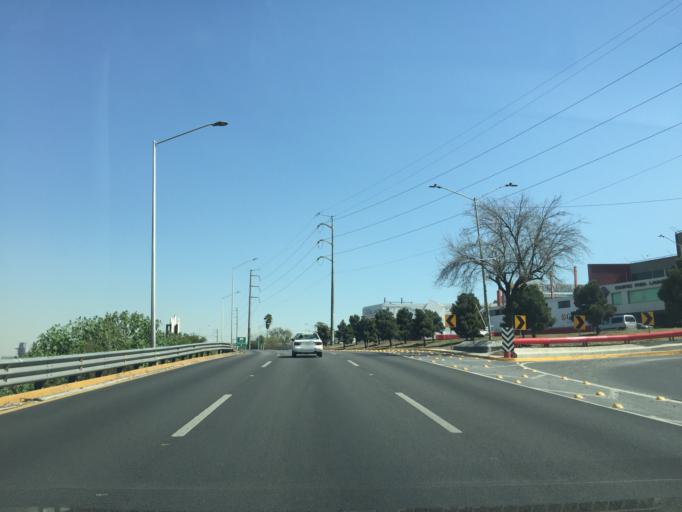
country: MX
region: Nuevo Leon
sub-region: Monterrey
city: Monterrey
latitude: 25.6673
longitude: -100.2971
